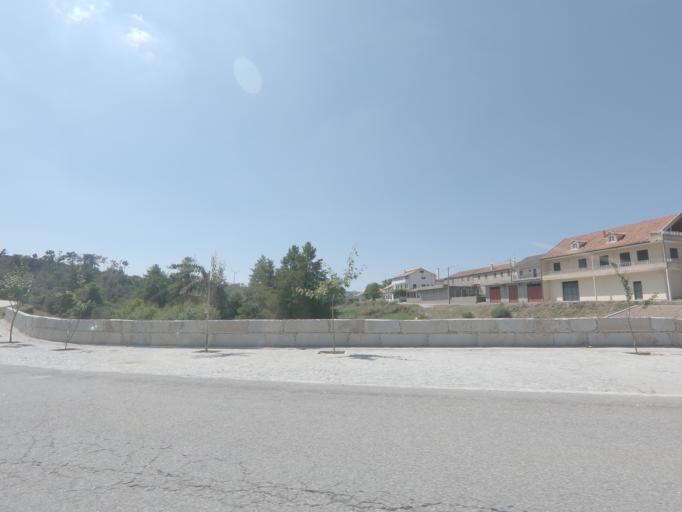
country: PT
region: Viseu
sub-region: Tarouca
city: Tarouca
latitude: 40.9925
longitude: -7.8243
